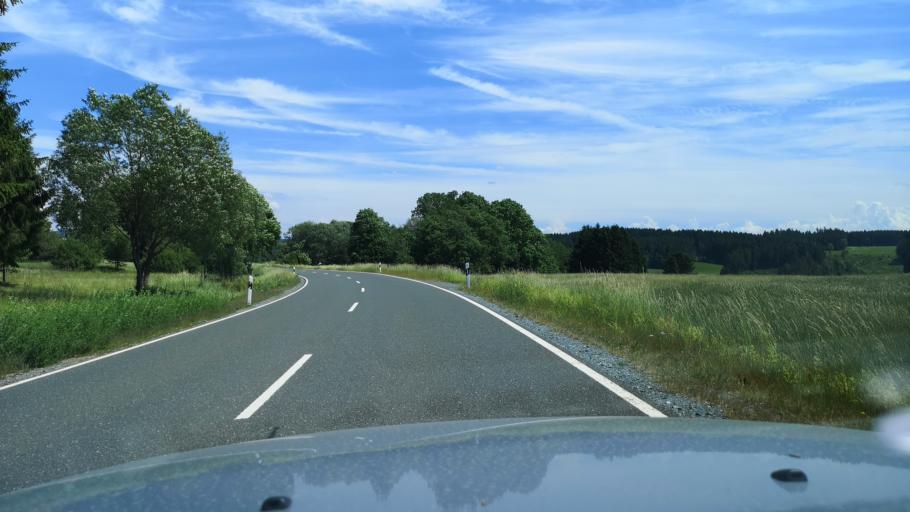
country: DE
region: Bavaria
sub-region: Upper Franconia
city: Teuschnitz
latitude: 50.3857
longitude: 11.3689
